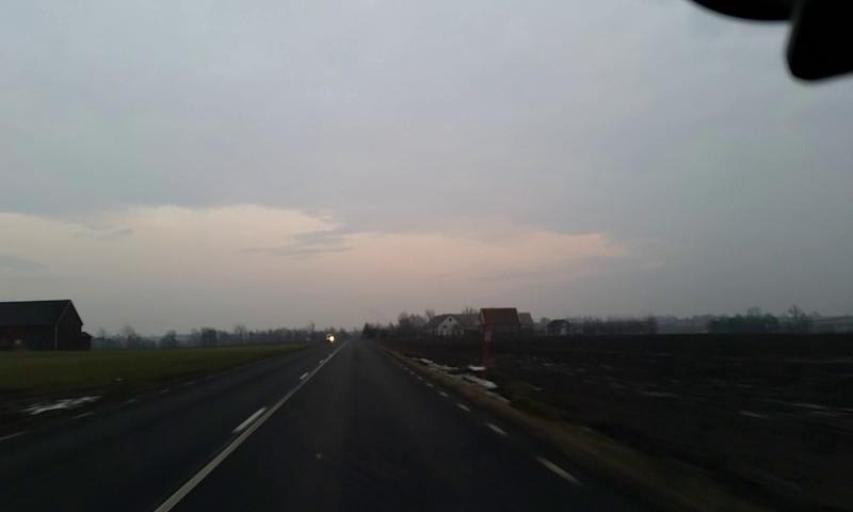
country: SE
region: Skane
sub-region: Angelholms Kommun
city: AEngelholm
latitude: 56.2731
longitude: 12.8857
